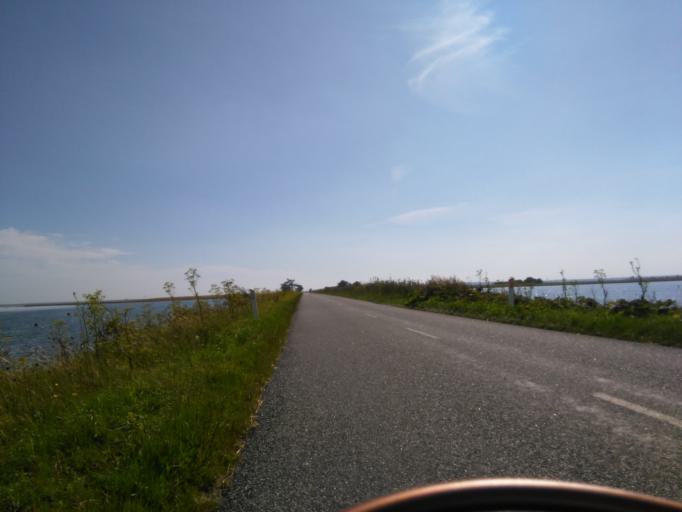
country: DK
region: Central Jutland
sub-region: Odder Kommune
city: Odder
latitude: 55.8696
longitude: 10.1182
